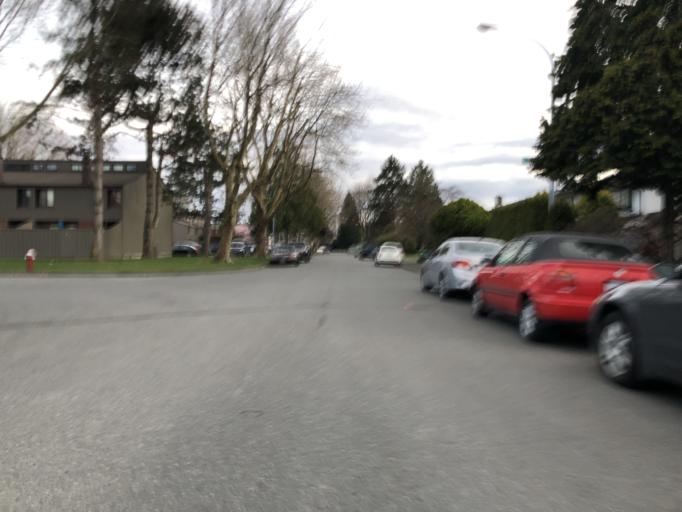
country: CA
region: British Columbia
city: Richmond
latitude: 49.1464
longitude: -123.1240
